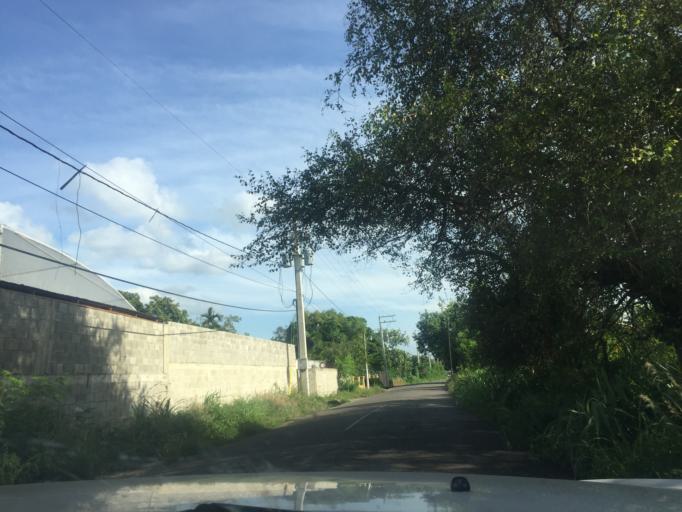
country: DO
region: Santiago
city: Tamboril
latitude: 19.4844
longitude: -70.6371
